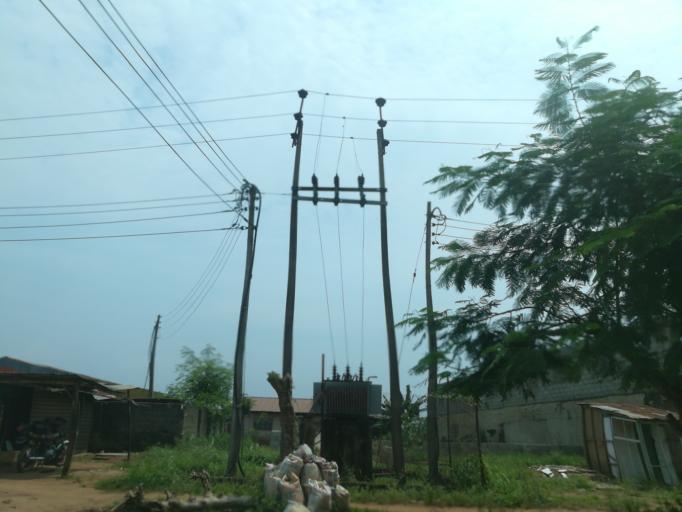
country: NG
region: Lagos
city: Ikorodu
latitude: 6.6040
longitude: 3.6031
